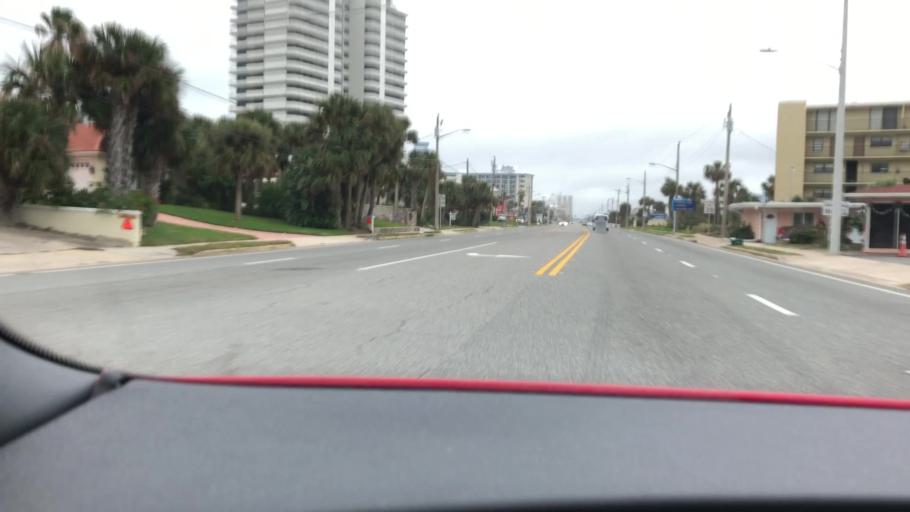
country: US
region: Florida
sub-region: Volusia County
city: Holly Hill
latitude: 29.2515
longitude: -81.0202
